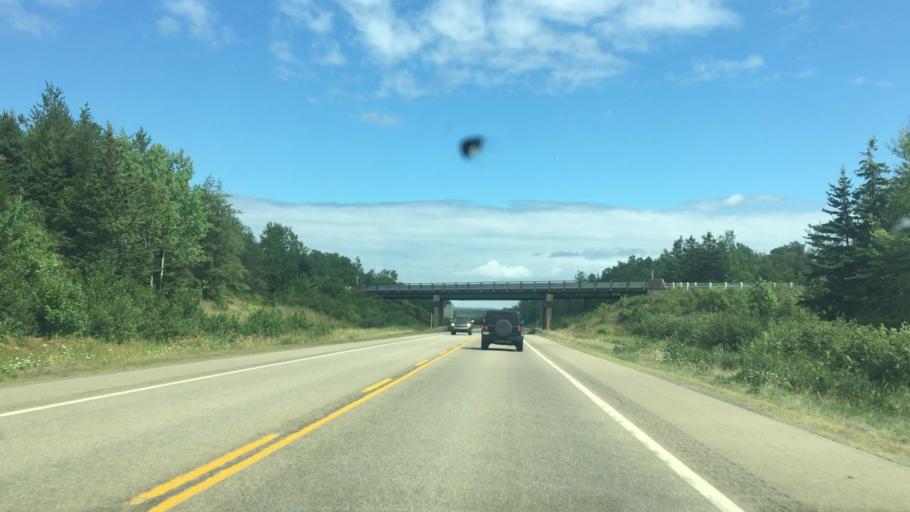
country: CA
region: Nova Scotia
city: Port Hawkesbury
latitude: 45.6289
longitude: -61.5939
